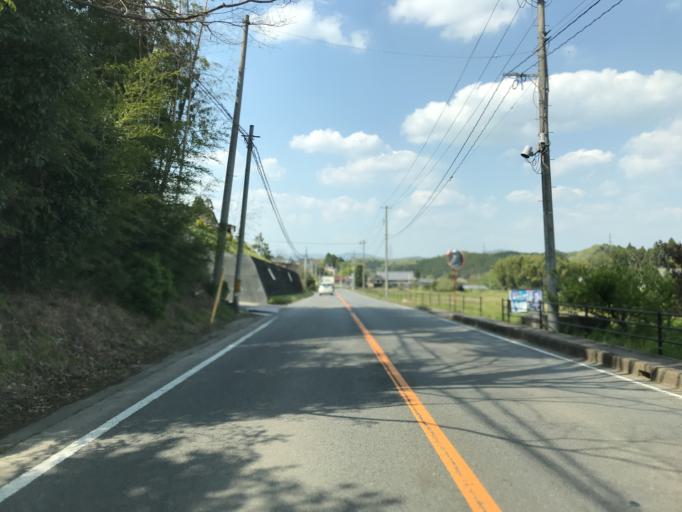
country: JP
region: Fukushima
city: Iwaki
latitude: 36.9448
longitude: 140.7682
